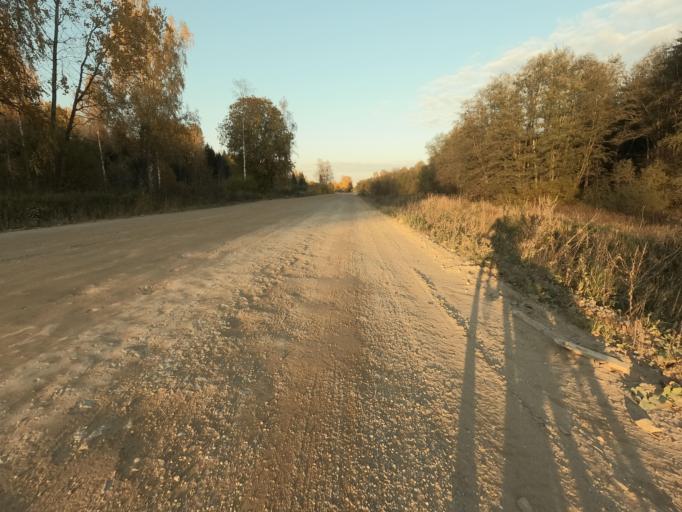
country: RU
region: Leningrad
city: Lyuban'
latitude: 59.0192
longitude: 31.0906
